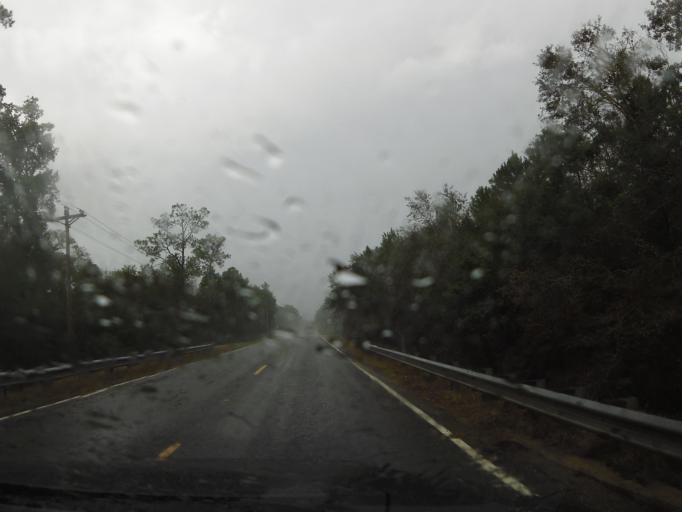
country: US
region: Florida
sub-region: Baker County
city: Macclenny
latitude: 30.3645
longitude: -82.1357
